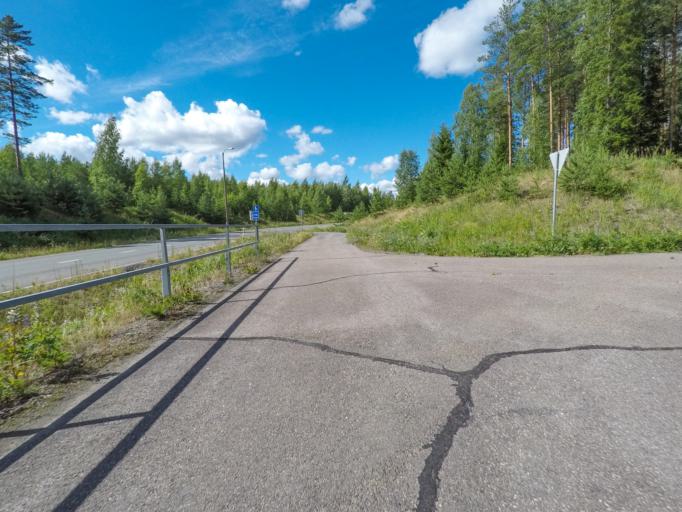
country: FI
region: South Karelia
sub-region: Lappeenranta
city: Joutseno
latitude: 61.0921
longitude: 28.3529
